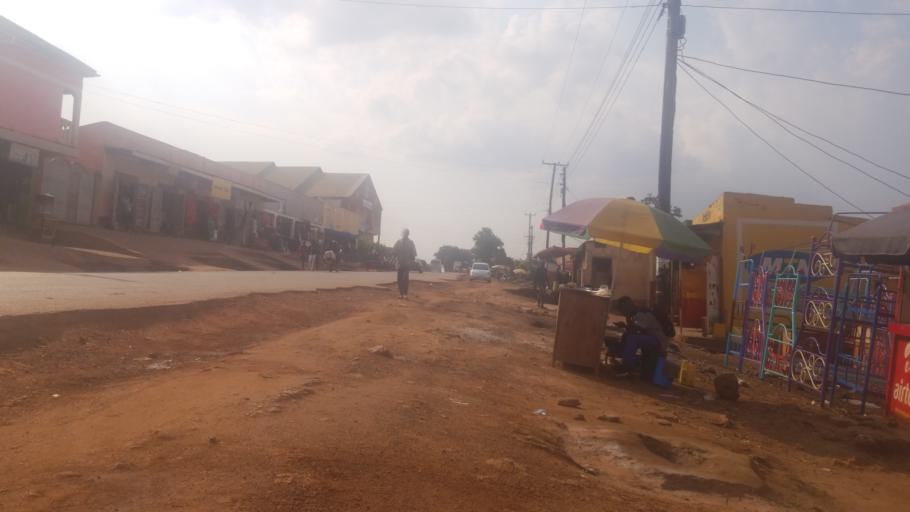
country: UG
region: Central Region
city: Kampala Central Division
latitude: 0.3360
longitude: 32.5557
